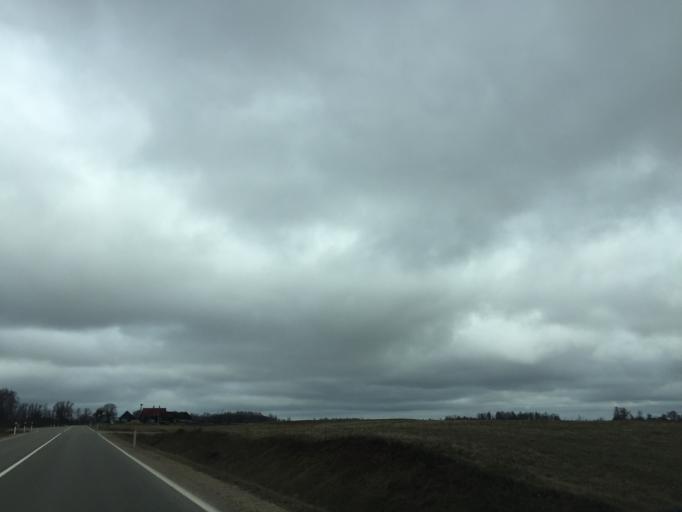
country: LV
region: Ilukste
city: Ilukste
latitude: 55.9957
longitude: 26.2869
